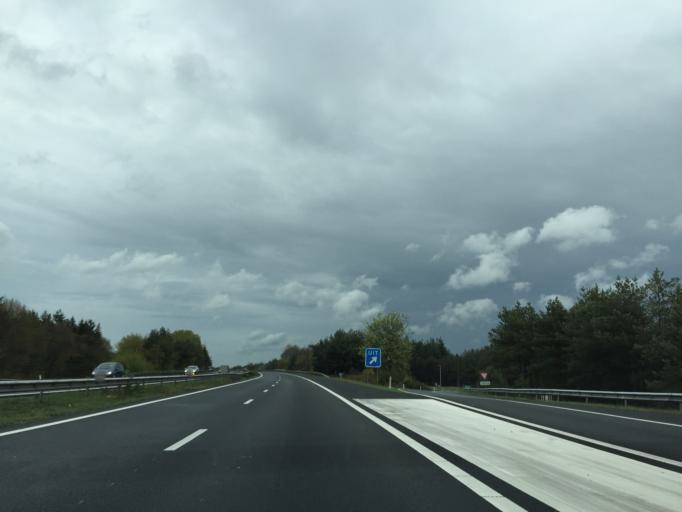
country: NL
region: Gelderland
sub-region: Gemeente Nunspeet
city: Nunspeet
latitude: 52.3728
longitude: 5.8198
